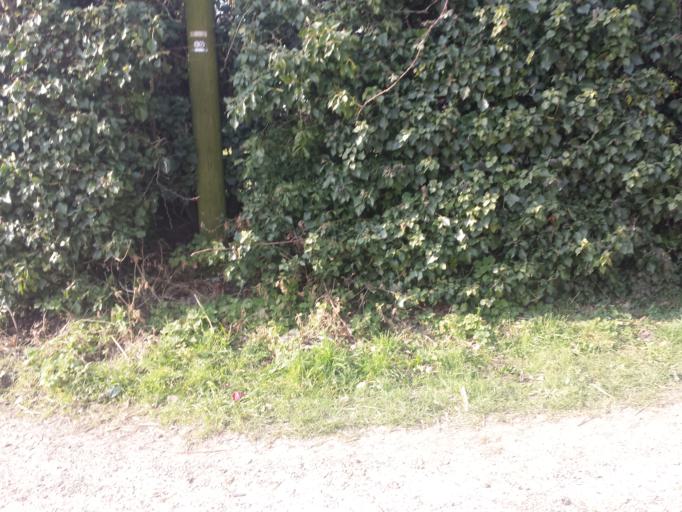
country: GB
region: England
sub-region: Essex
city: Little Clacton
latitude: 51.8816
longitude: 1.1582
